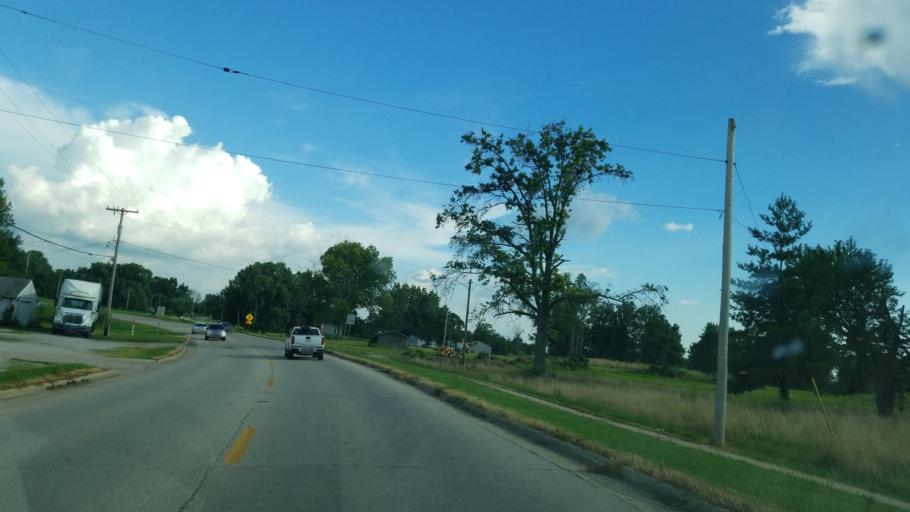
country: US
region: Illinois
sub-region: Marion County
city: Sandoval
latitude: 38.6080
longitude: -89.1156
